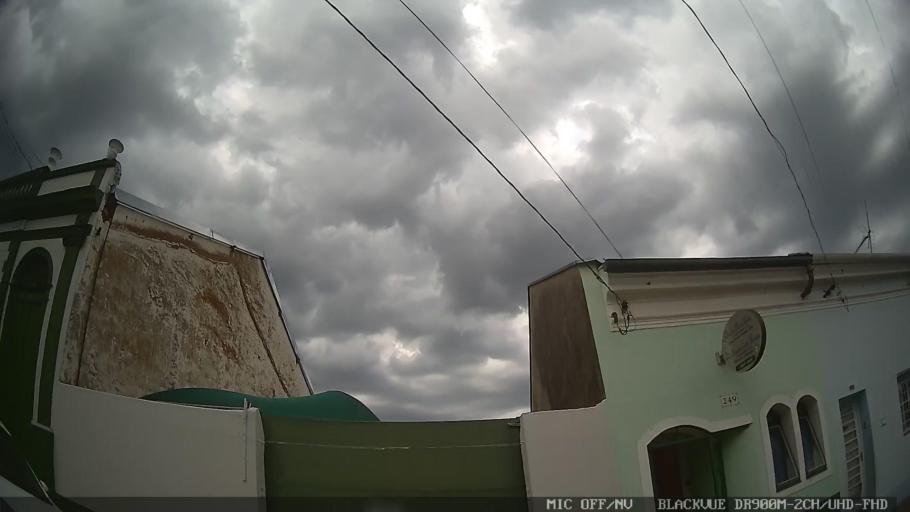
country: BR
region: Sao Paulo
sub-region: Amparo
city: Amparo
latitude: -22.7023
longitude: -46.7630
